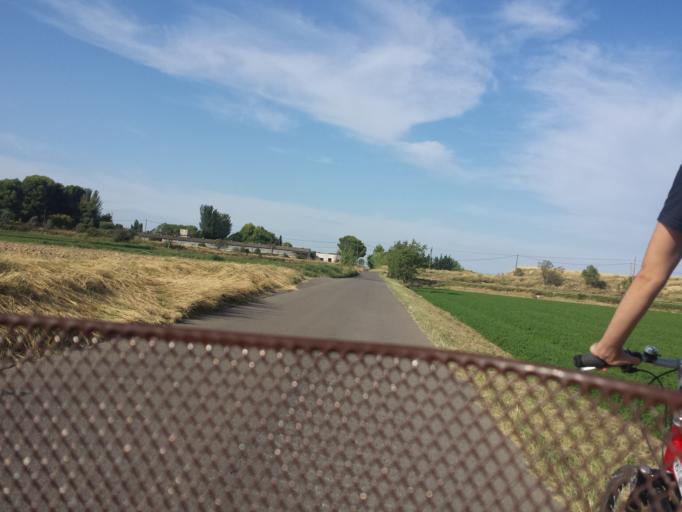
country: ES
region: Aragon
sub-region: Provincia de Zaragoza
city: Zaragoza
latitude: 41.6971
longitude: -0.8597
